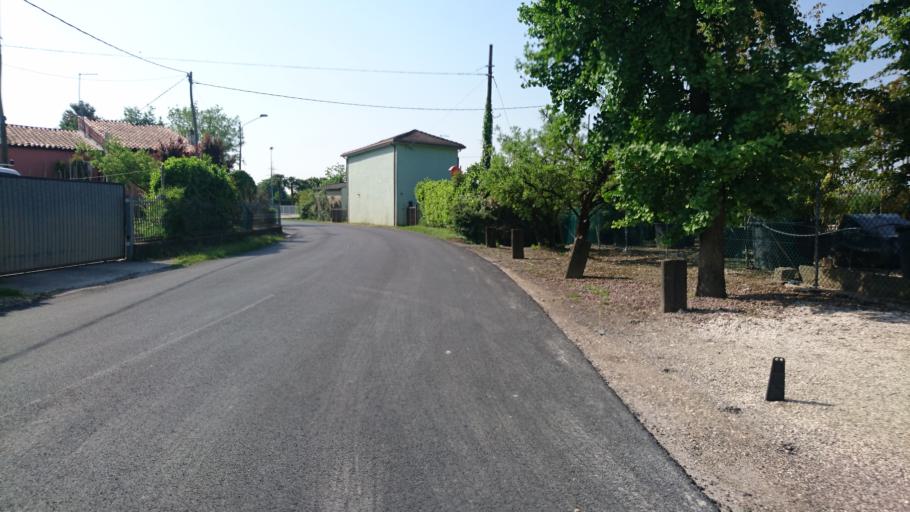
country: IT
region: Veneto
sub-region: Provincia di Padova
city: Saonara
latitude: 45.3729
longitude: 11.9956
